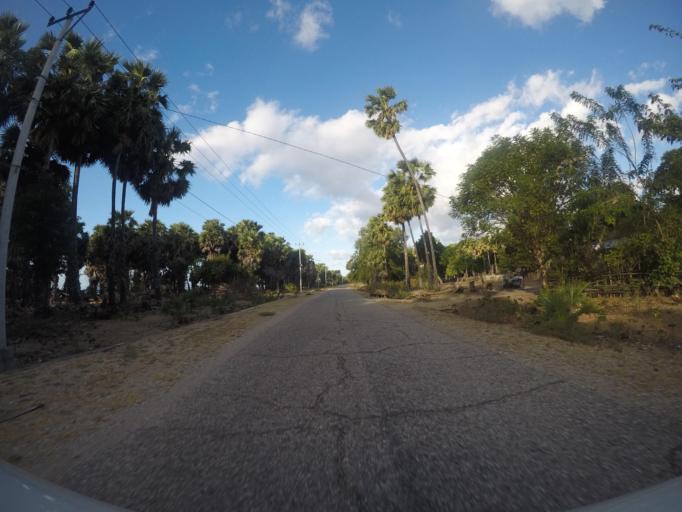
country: TL
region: Lautem
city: Lospalos
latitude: -8.3368
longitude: 126.9418
